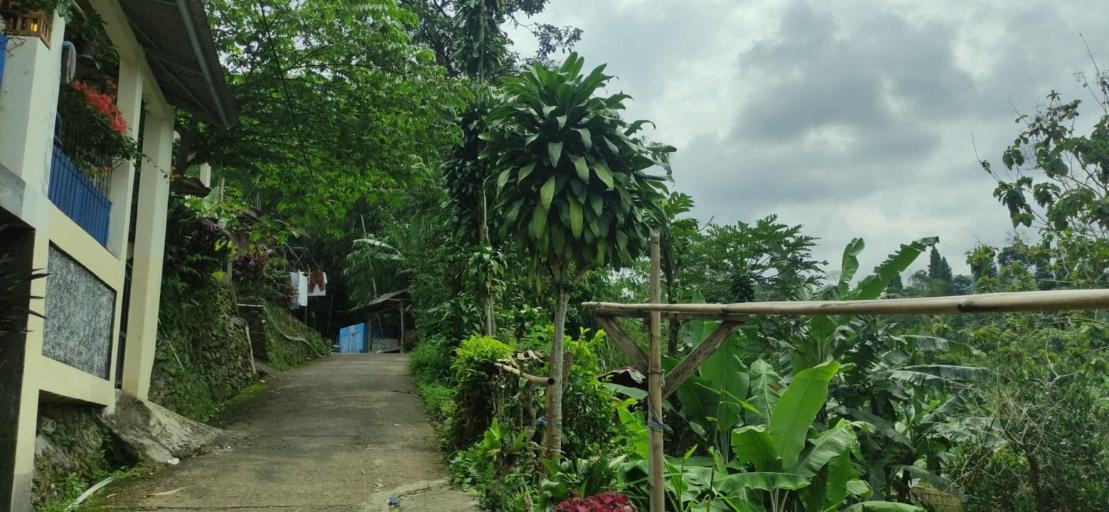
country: ID
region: West Java
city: Caringin
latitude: -6.6426
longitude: 106.9008
